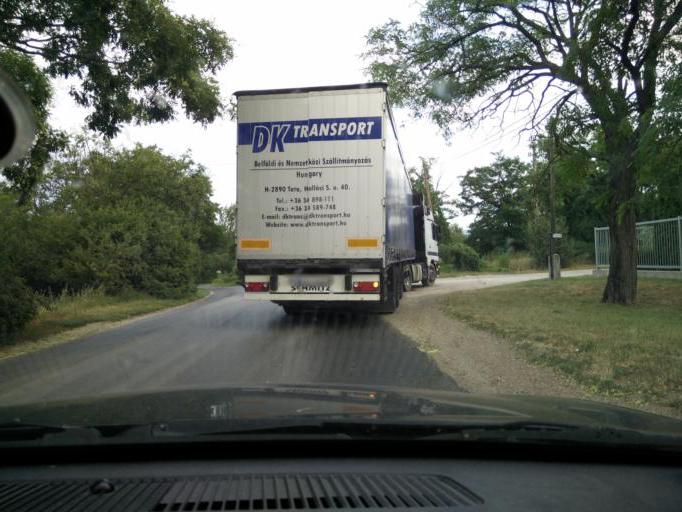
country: HU
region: Komarom-Esztergom
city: Baj
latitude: 47.6581
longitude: 18.3440
